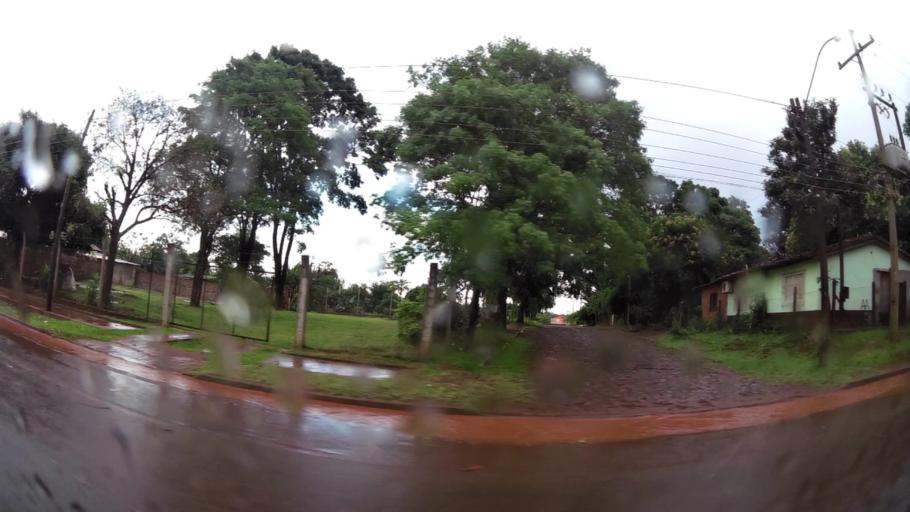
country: PY
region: Alto Parana
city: Presidente Franco
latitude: -25.5583
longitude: -54.6611
